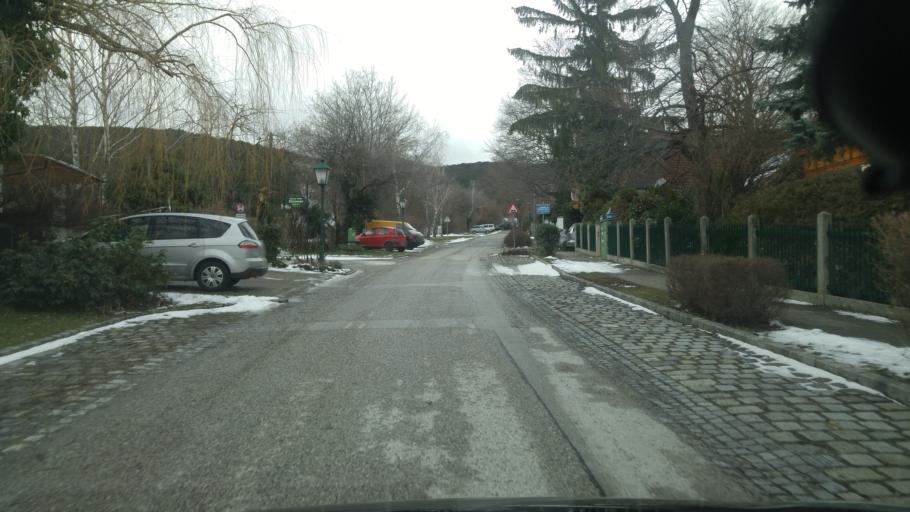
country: AT
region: Lower Austria
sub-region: Politischer Bezirk Baden
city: Bad Voslau
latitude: 47.9853
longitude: 16.2032
